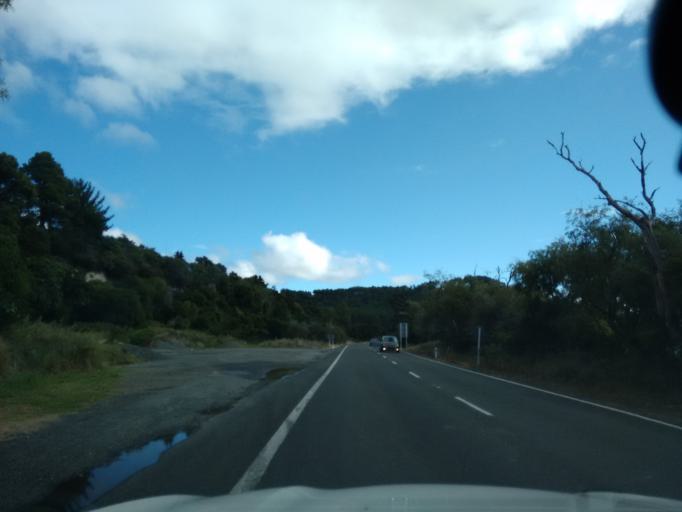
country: NZ
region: Waikato
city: Turangi
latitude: -38.8854
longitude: 175.9647
